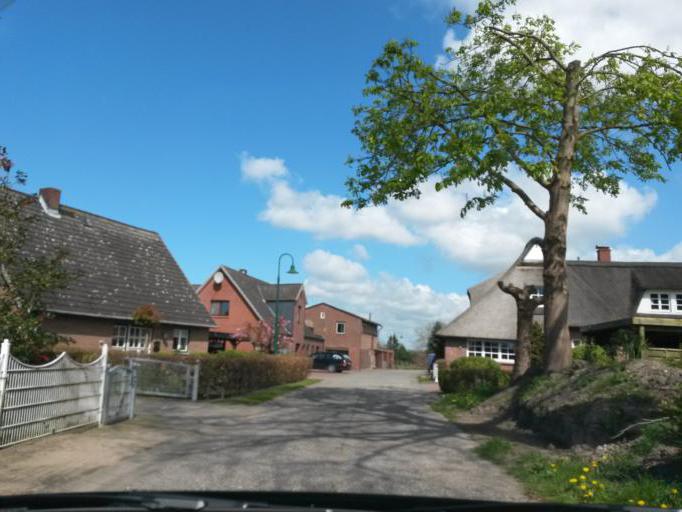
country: DE
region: Schleswig-Holstein
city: Haseldorf
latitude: 53.6398
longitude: 9.5728
